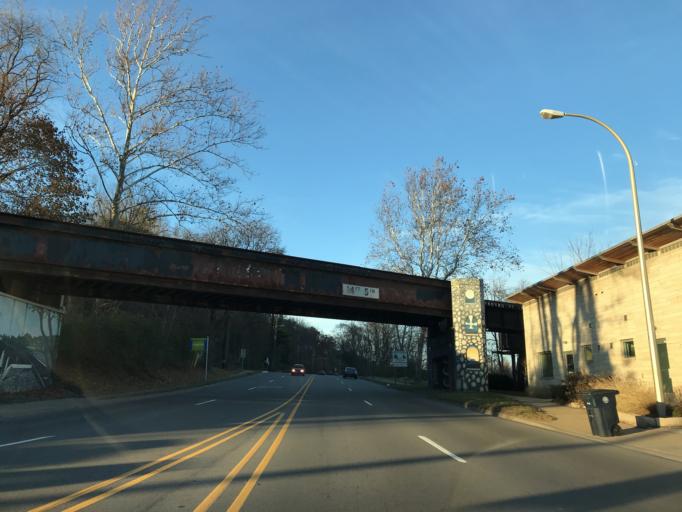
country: US
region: Michigan
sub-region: Washtenaw County
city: Ann Arbor
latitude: 42.2898
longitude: -83.7470
